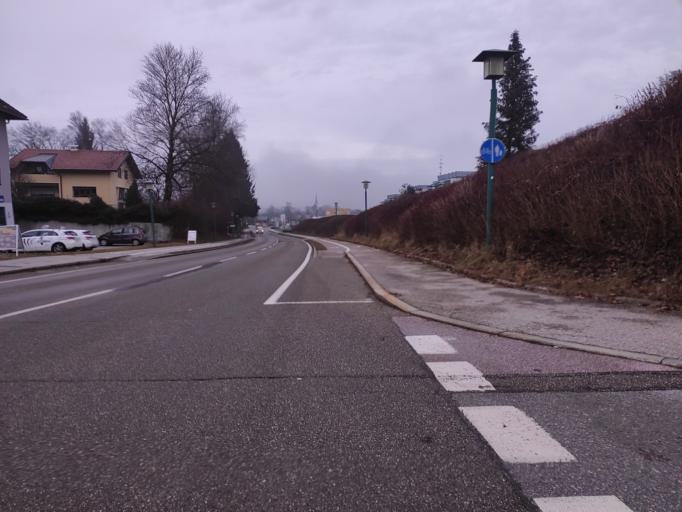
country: AT
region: Salzburg
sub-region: Politischer Bezirk Salzburg-Umgebung
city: Neumarkt am Wallersee
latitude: 47.9383
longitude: 13.2237
